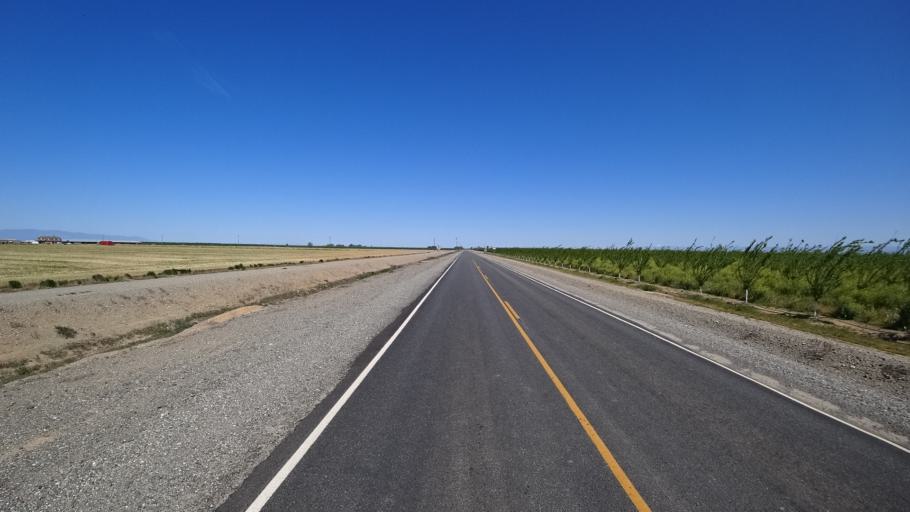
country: US
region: California
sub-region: Glenn County
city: Orland
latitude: 39.6534
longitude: -122.1409
